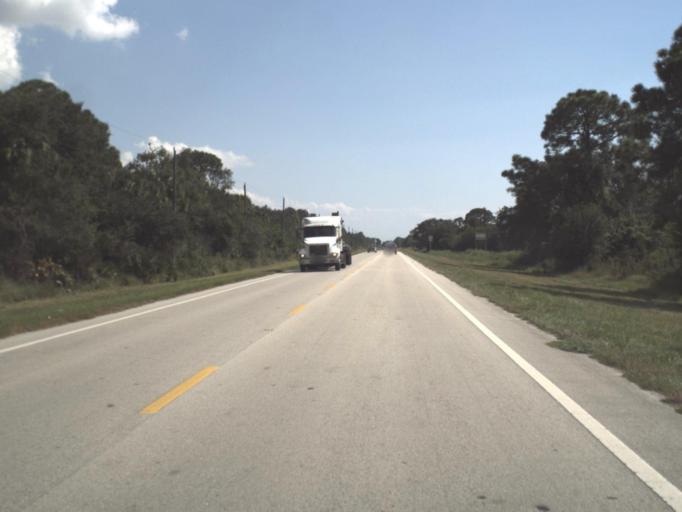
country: US
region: Florida
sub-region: Okeechobee County
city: Okeechobee
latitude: 27.2789
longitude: -80.8761
